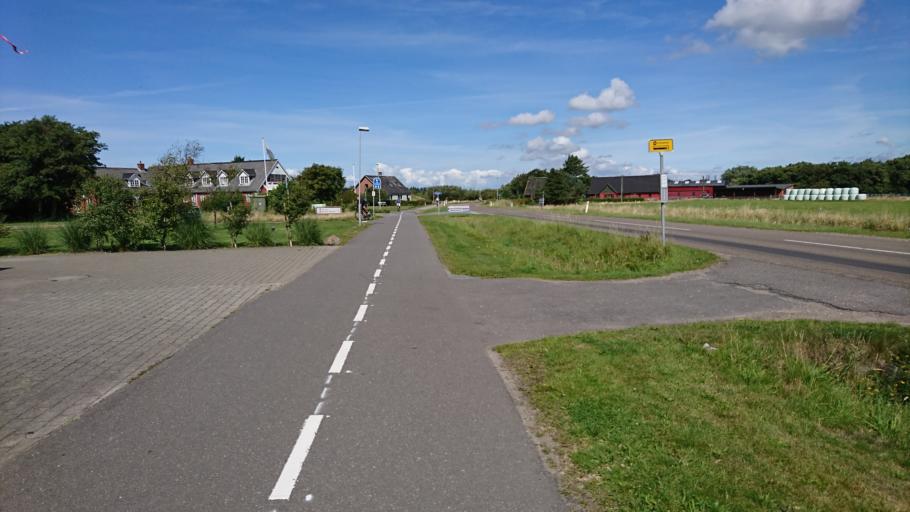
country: DK
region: South Denmark
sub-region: Fano Kommune
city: Nordby
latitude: 55.4308
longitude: 8.3944
